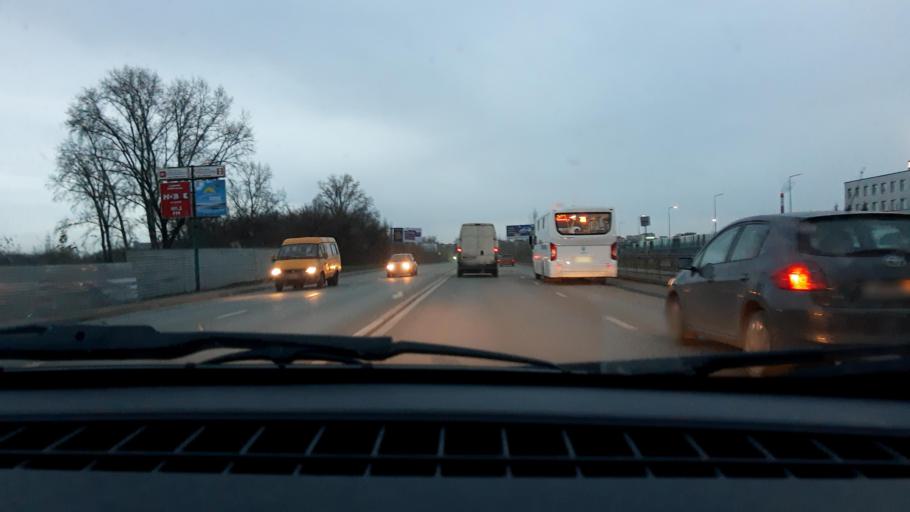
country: RU
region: Bashkortostan
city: Ufa
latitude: 54.7955
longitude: 56.0769
